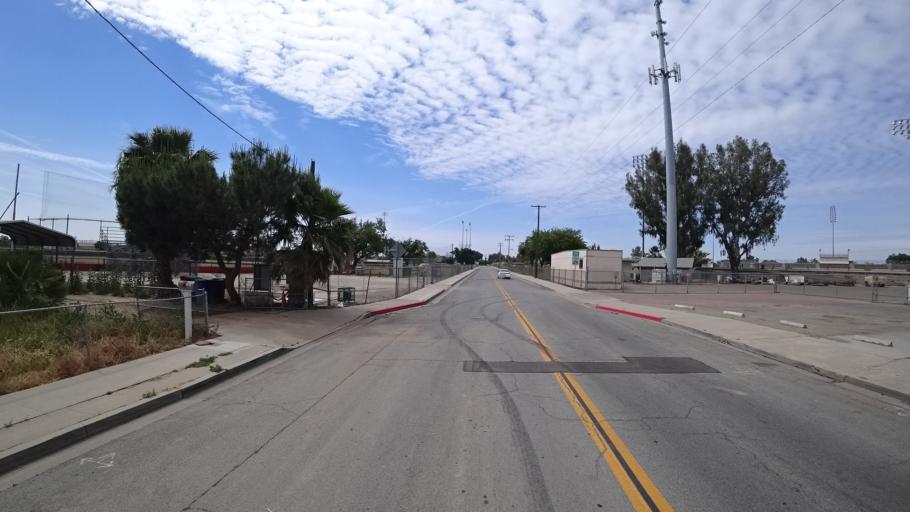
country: US
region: California
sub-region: Kings County
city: Hanford
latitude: 36.3462
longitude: -119.6415
